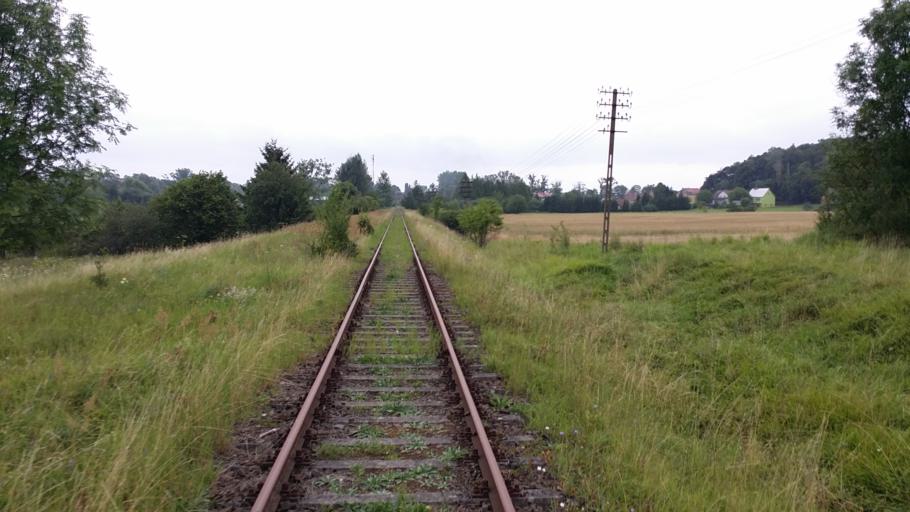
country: PL
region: West Pomeranian Voivodeship
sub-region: Powiat choszczenski
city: Drawno
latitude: 53.2106
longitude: 15.7646
